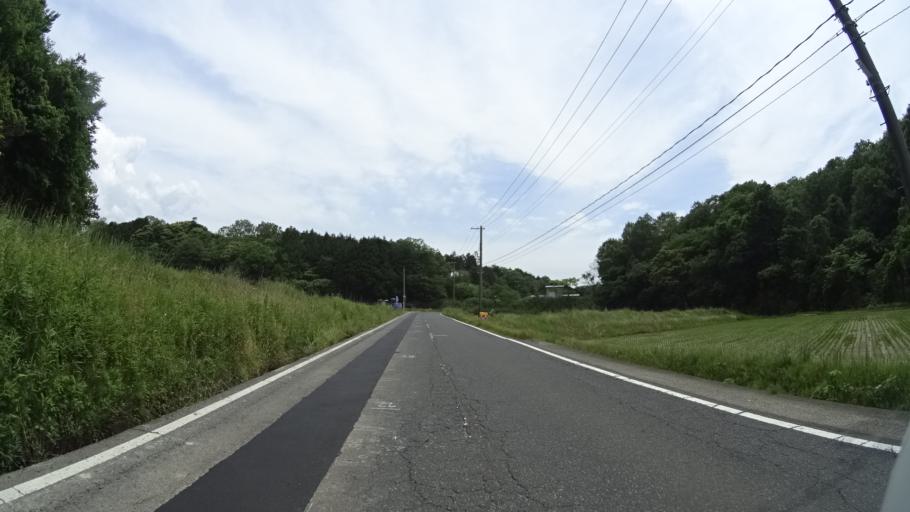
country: JP
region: Kyoto
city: Miyazu
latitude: 35.6823
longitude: 135.0670
